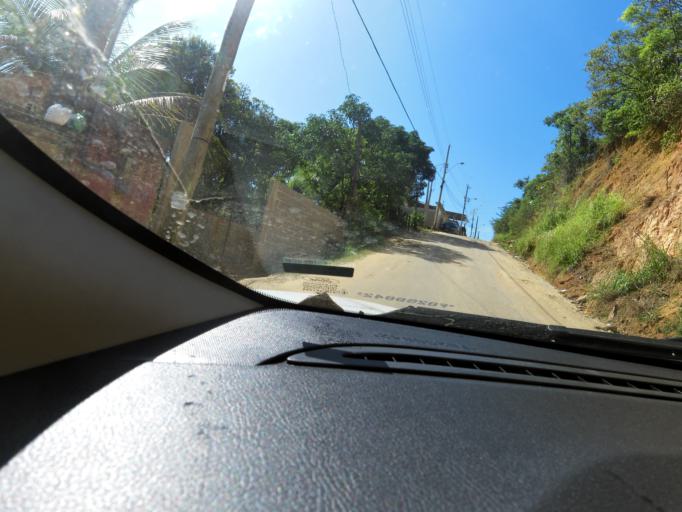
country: BR
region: Espirito Santo
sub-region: Guarapari
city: Guarapari
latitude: -20.6569
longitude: -40.5211
